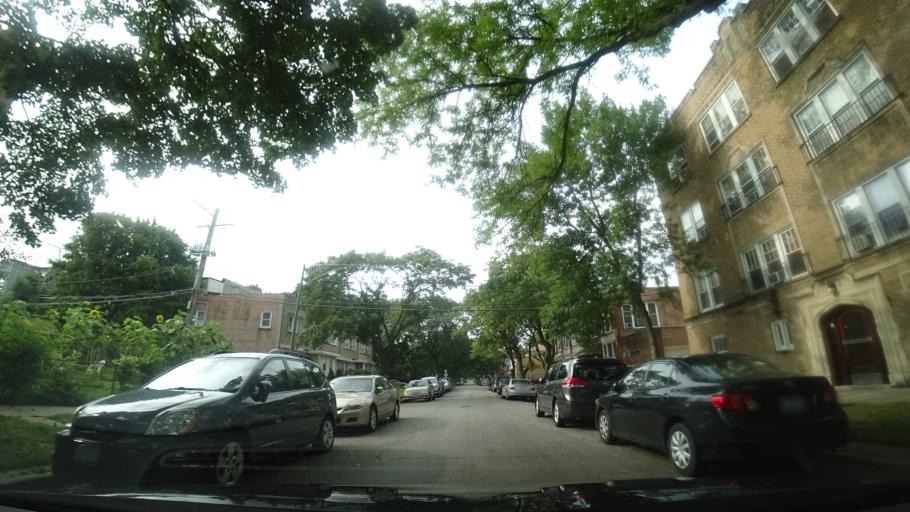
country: US
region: Illinois
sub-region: Cook County
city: Evanston
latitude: 42.0102
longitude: -87.6974
